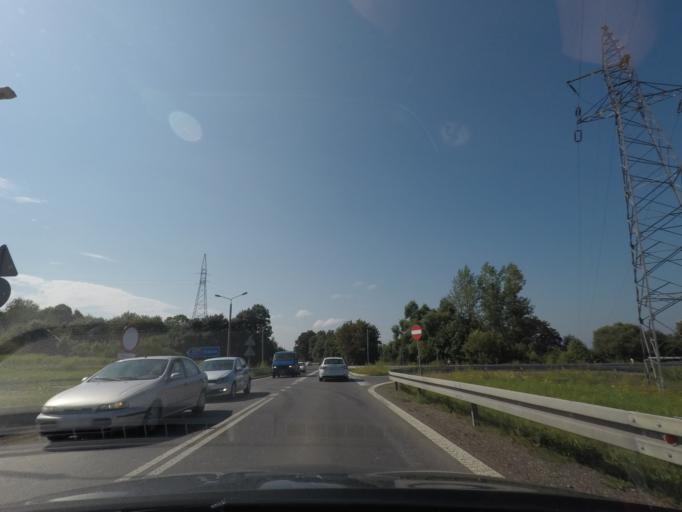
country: PL
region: Lesser Poland Voivodeship
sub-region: Powiat chrzanowski
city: Chrzanow
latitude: 50.1513
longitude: 19.3987
